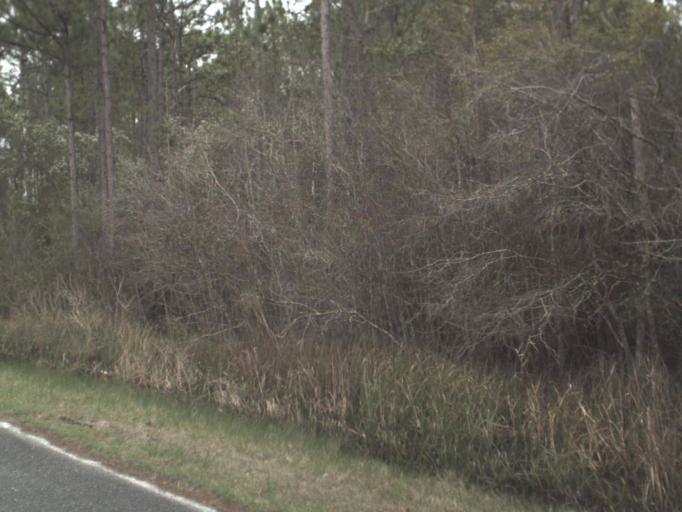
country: US
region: Florida
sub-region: Franklin County
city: Eastpoint
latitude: 29.8287
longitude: -84.8647
